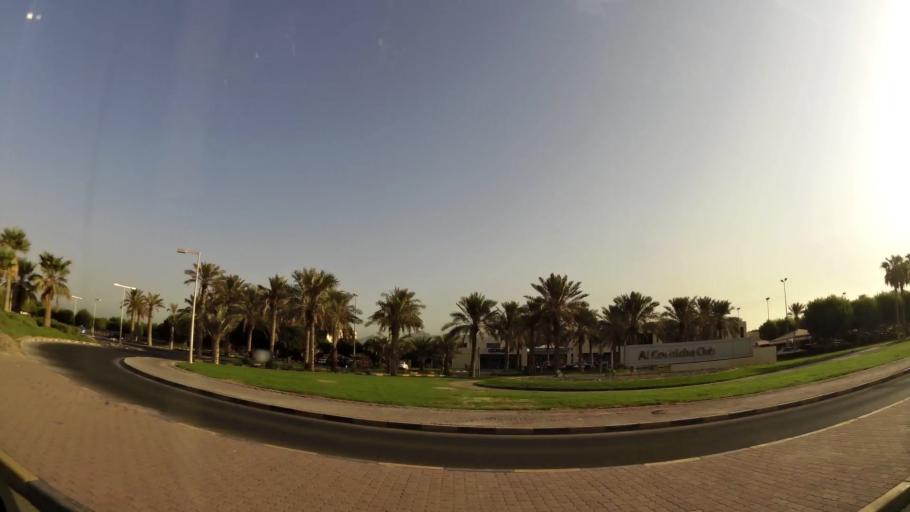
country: KW
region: Muhafazat Hawalli
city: Hawalli
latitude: 29.3432
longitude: 48.0464
